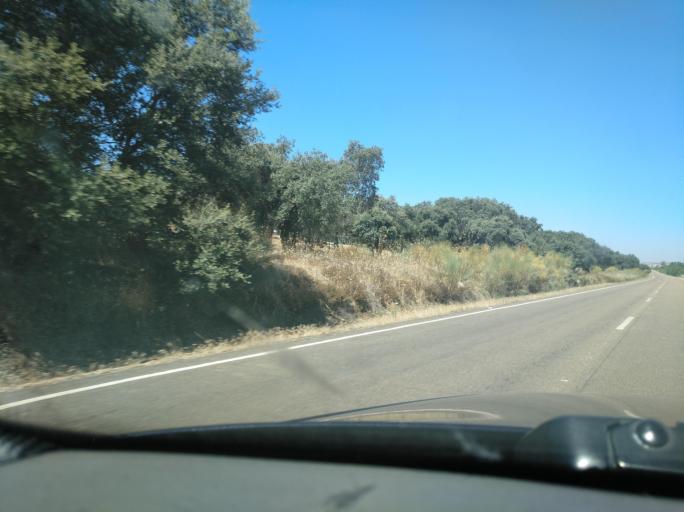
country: ES
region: Extremadura
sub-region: Provincia de Badajoz
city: Olivenza
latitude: 38.7146
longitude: -7.1937
